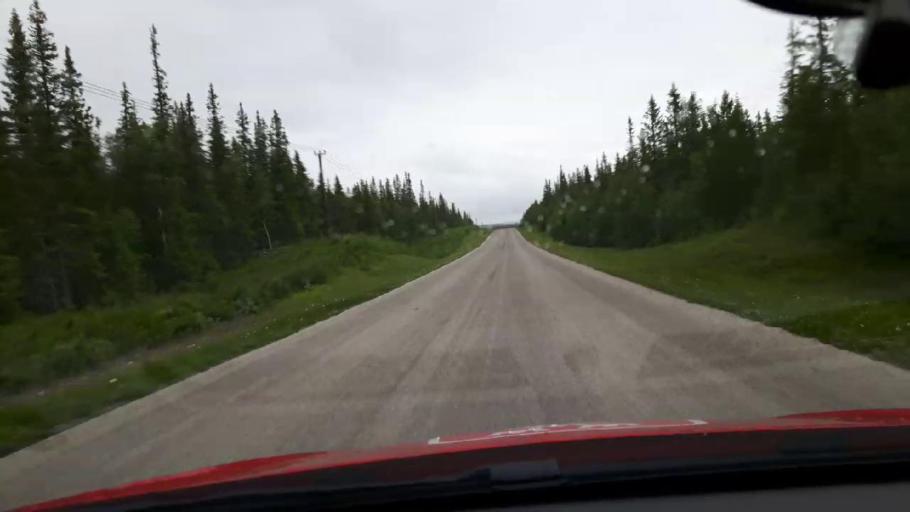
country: NO
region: Nord-Trondelag
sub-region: Meraker
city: Meraker
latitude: 63.2740
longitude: 12.3636
